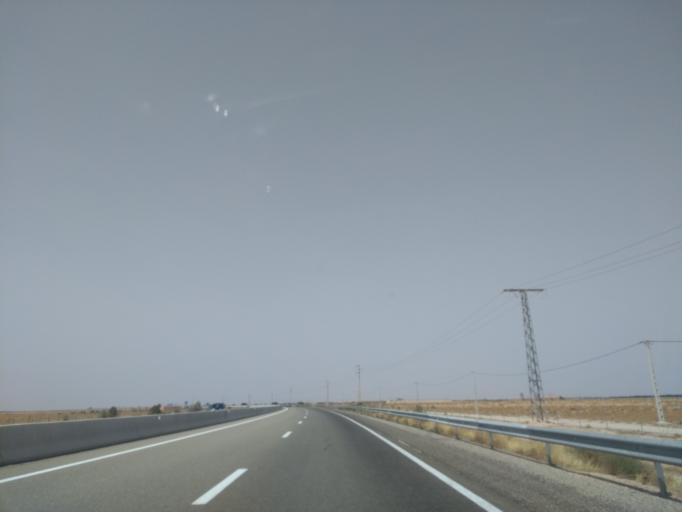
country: MA
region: Marrakech-Tensift-Al Haouz
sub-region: Chichaoua
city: Chichaoua
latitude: 31.4534
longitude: -8.7035
